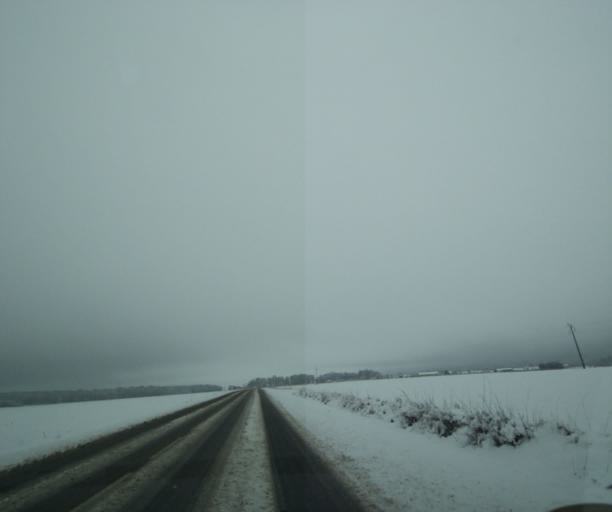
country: FR
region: Champagne-Ardenne
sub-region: Departement de la Haute-Marne
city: Wassy
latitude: 48.5569
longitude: 4.9258
